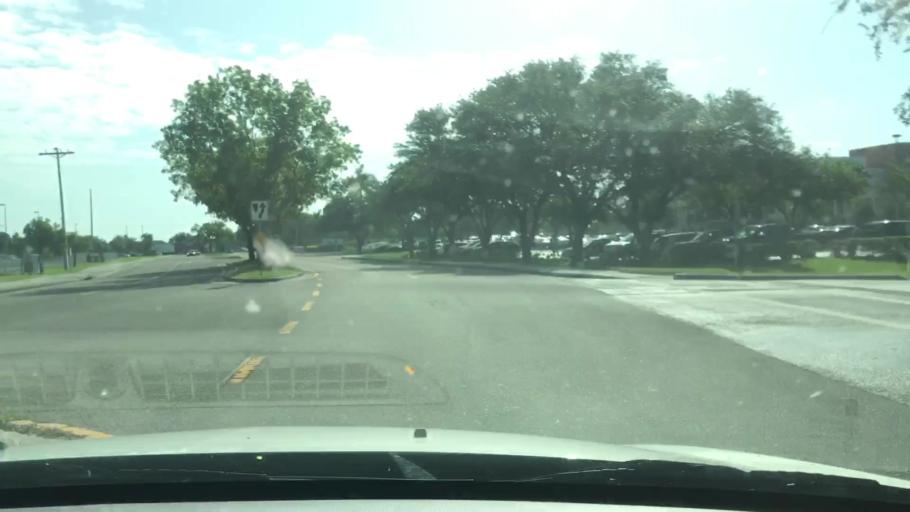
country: US
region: Florida
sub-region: Lee County
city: Lochmoor Waterway Estates
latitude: 26.6413
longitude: -81.9442
